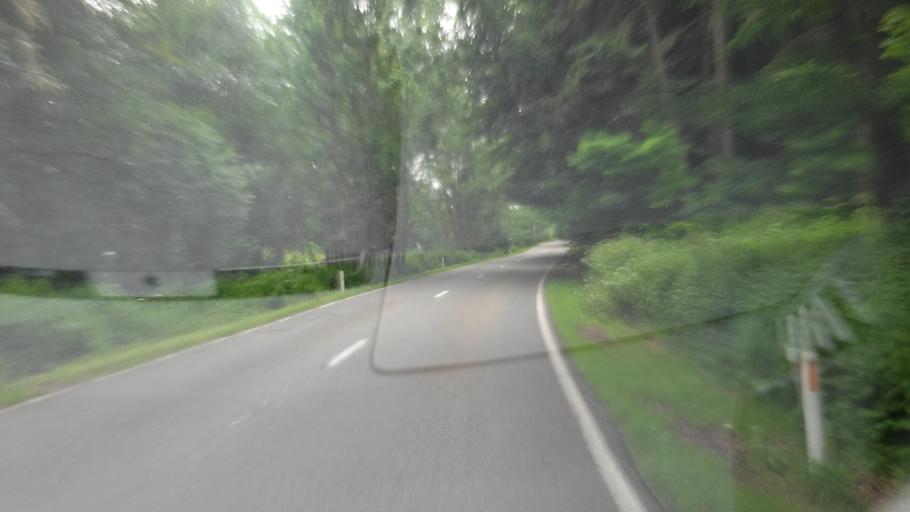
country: LU
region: Luxembourg
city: Eischen
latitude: 49.6952
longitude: 5.8522
